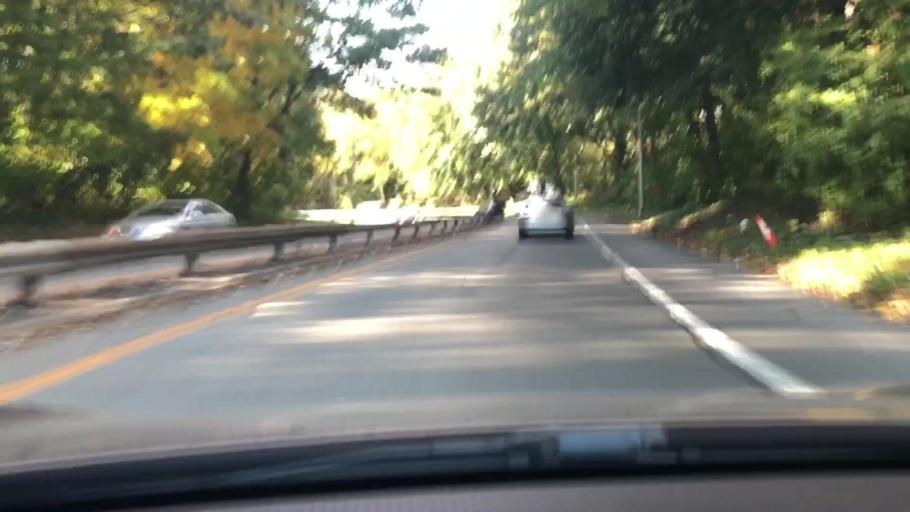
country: US
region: New York
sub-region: Westchester County
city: Bronxville
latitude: 40.9239
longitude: -73.8233
